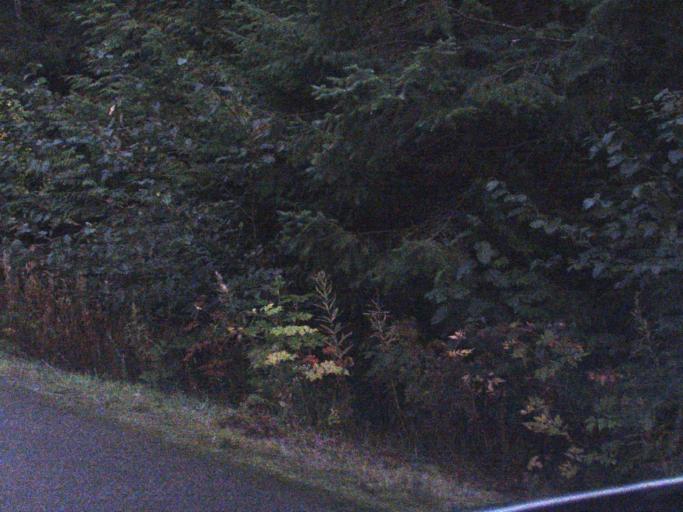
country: US
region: Washington
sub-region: Snohomish County
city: Darrington
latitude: 48.7042
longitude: -120.9514
